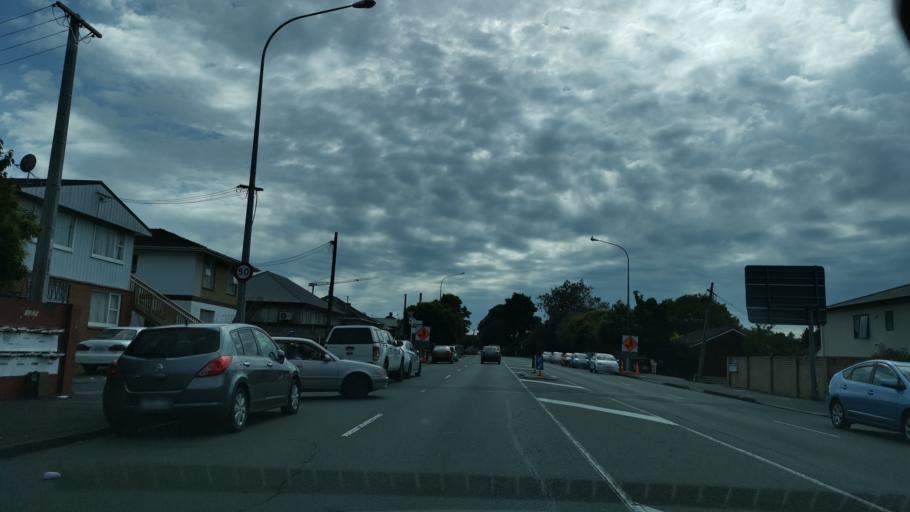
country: NZ
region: Auckland
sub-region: Auckland
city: Rosebank
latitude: -36.8960
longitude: 174.7029
